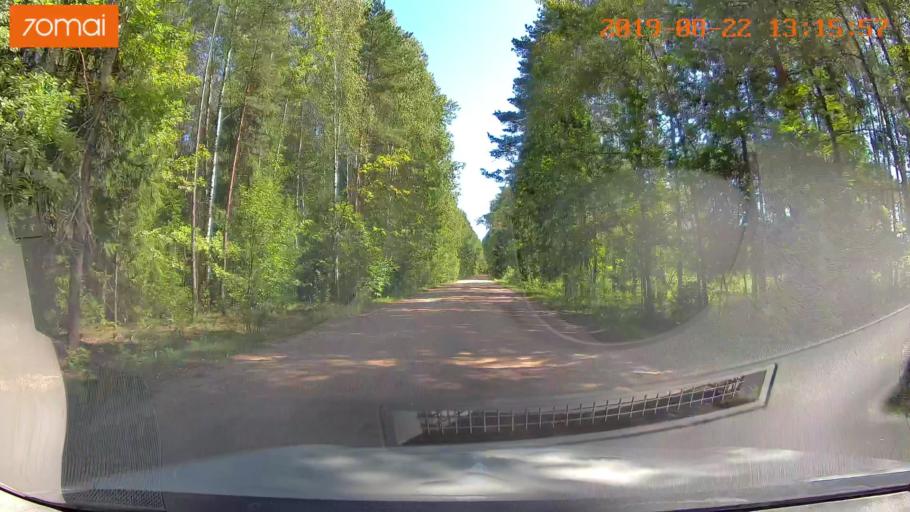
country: BY
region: Minsk
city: Prawdzinski
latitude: 53.2577
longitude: 27.9046
